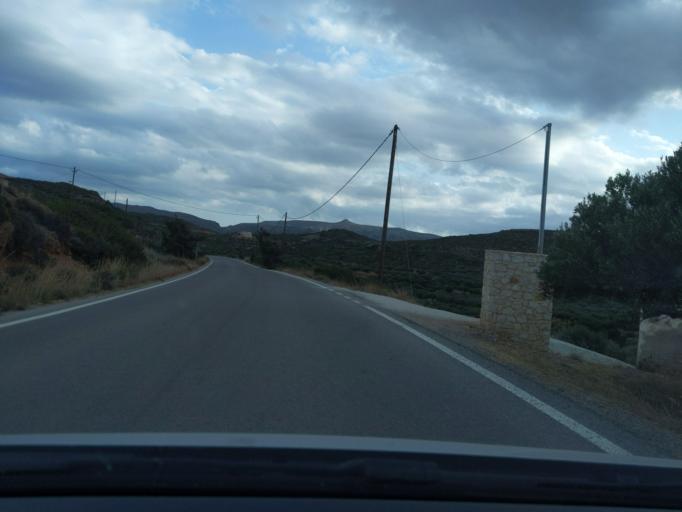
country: GR
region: Crete
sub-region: Nomos Lasithiou
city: Palekastro
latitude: 35.2272
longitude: 26.2560
